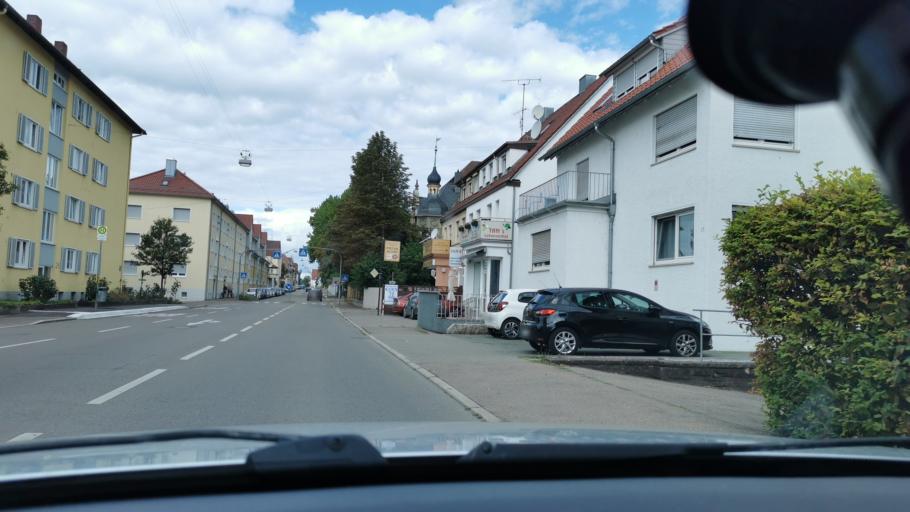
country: DE
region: Baden-Wuerttemberg
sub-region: Regierungsbezirk Stuttgart
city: Goeppingen
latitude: 48.7091
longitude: 9.6574
